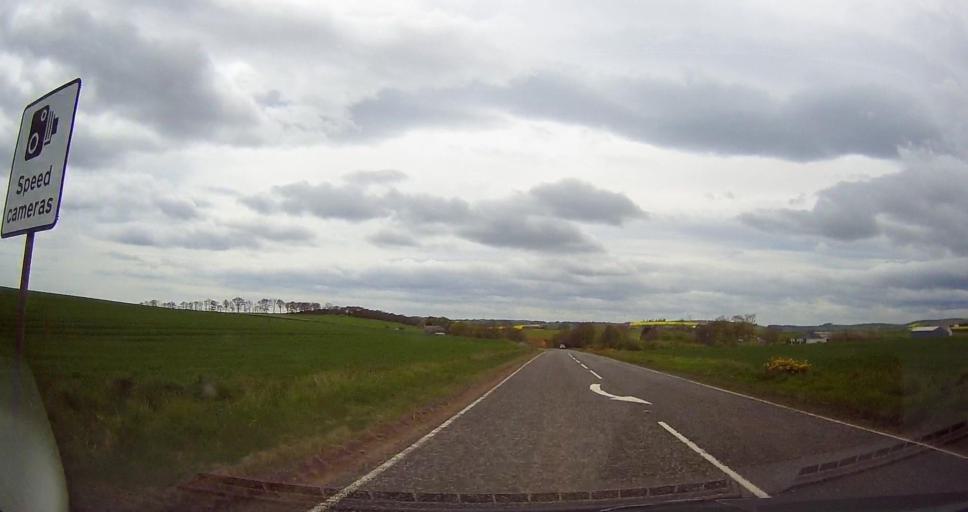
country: GB
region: Scotland
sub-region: Aberdeenshire
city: Stonehaven
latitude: 56.9152
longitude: -2.2144
